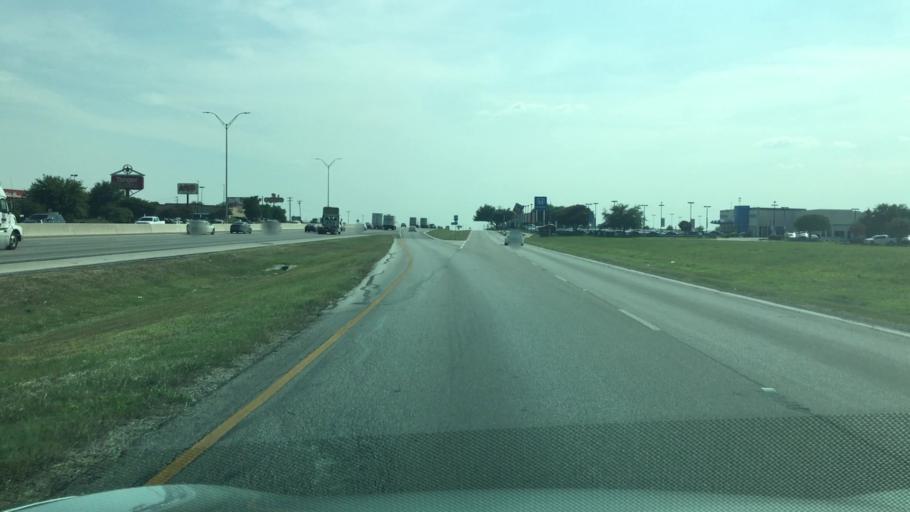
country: US
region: Texas
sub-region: Hays County
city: San Marcos
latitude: 29.8254
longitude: -97.9886
